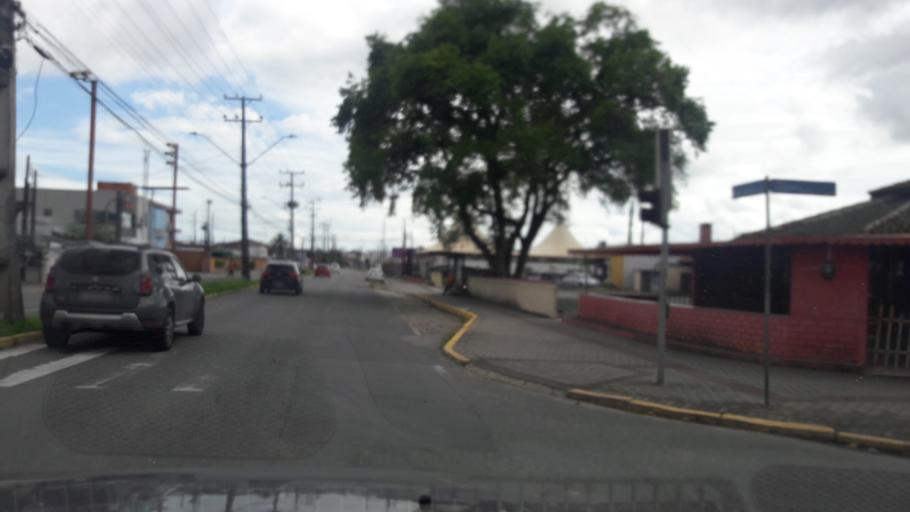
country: BR
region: Santa Catarina
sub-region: Joinville
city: Joinville
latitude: -26.3161
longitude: -48.8406
